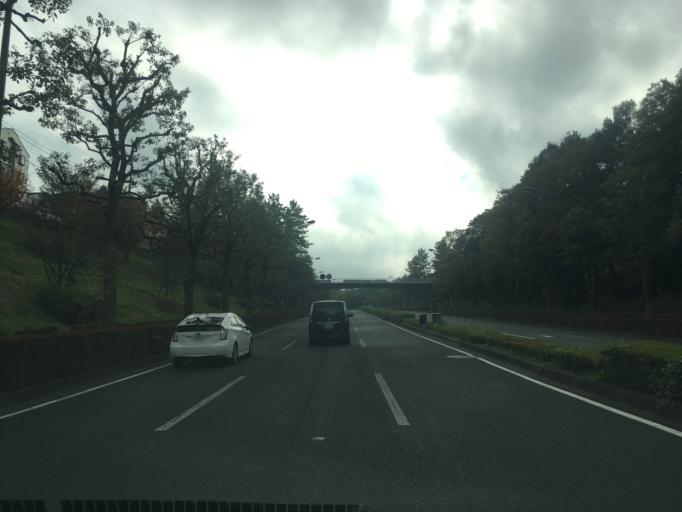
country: JP
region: Tokyo
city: Hino
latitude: 35.6176
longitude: 139.4223
